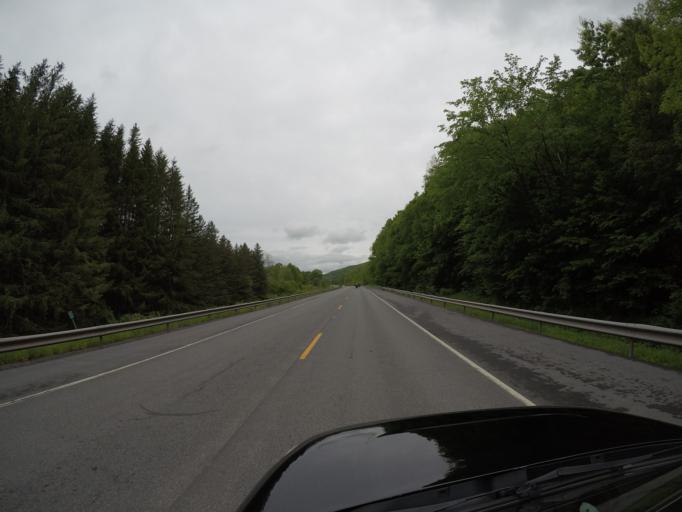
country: US
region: New York
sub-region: Sullivan County
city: Livingston Manor
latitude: 42.1291
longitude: -74.6668
